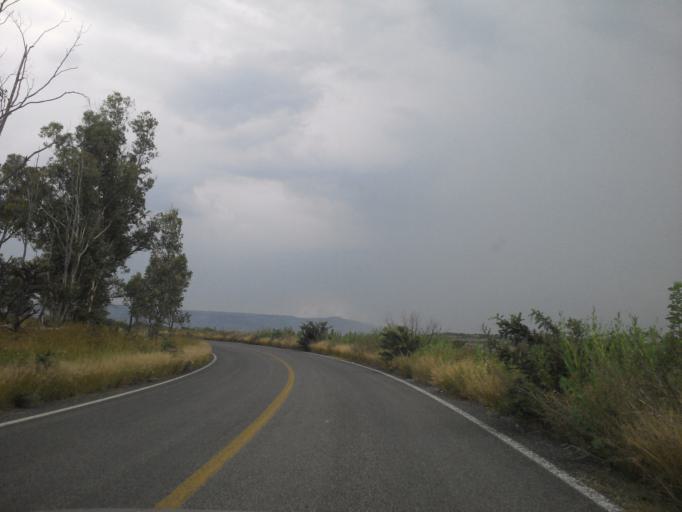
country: MX
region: Jalisco
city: San Diego de Alejandria
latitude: 20.8653
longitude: -102.0821
